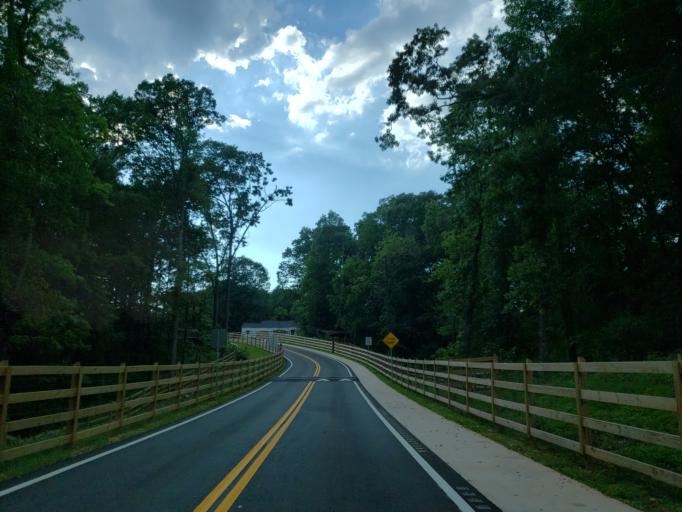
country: US
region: Georgia
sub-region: Fulton County
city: Roswell
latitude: 34.0574
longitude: -84.4332
